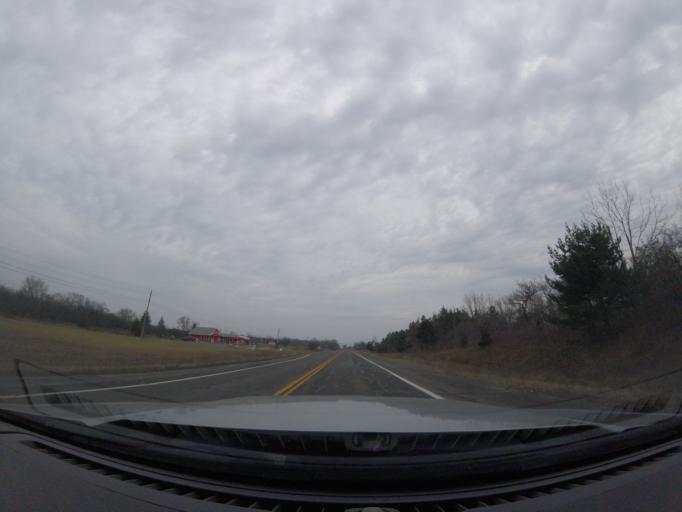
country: US
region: New York
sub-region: Yates County
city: Dundee
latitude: 42.5211
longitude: -76.9209
